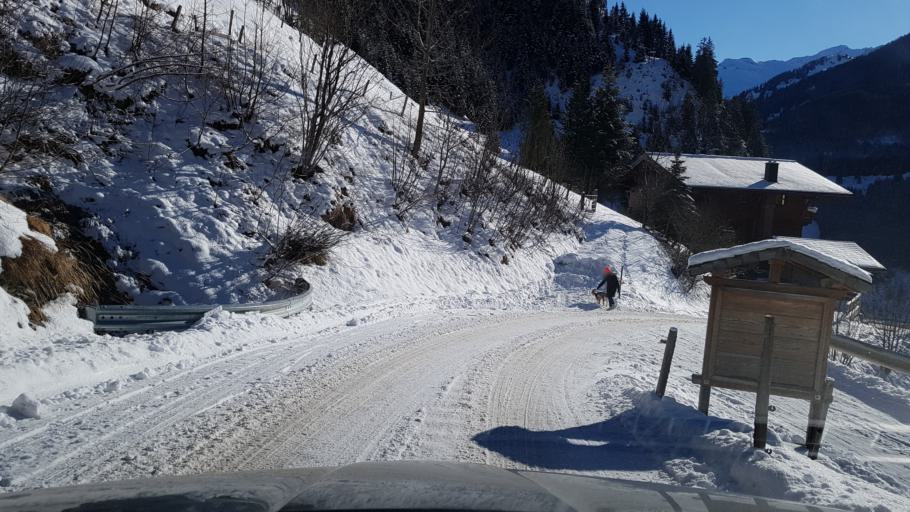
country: AT
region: Salzburg
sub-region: Politischer Bezirk Sankt Johann im Pongau
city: Huttschlag
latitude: 47.1721
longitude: 13.2663
